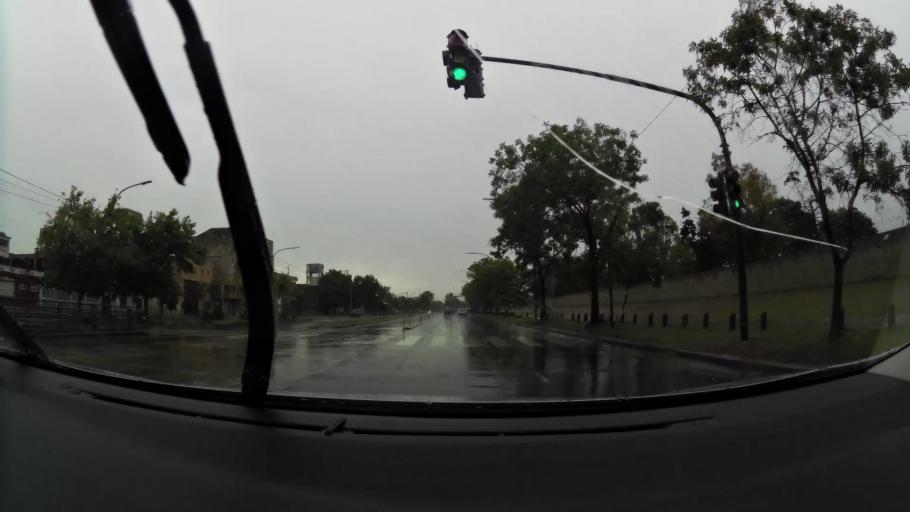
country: AR
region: Buenos Aires F.D.
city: Villa Lugano
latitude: -34.6536
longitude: -58.4353
